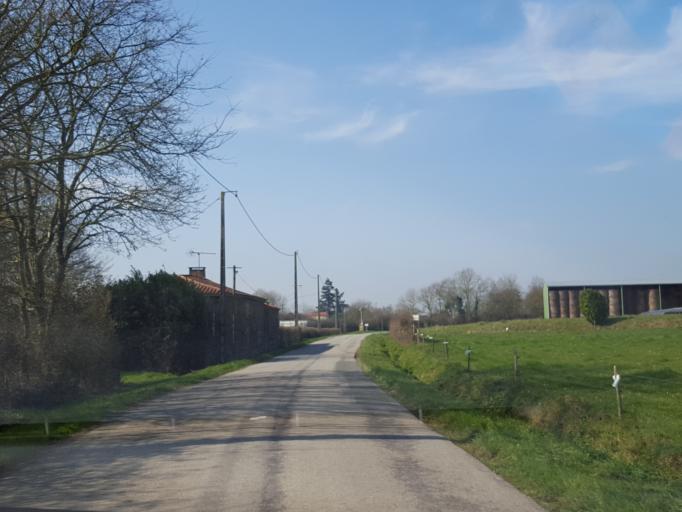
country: FR
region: Pays de la Loire
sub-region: Departement de la Vendee
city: Vendrennes
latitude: 46.8294
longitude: -1.1483
